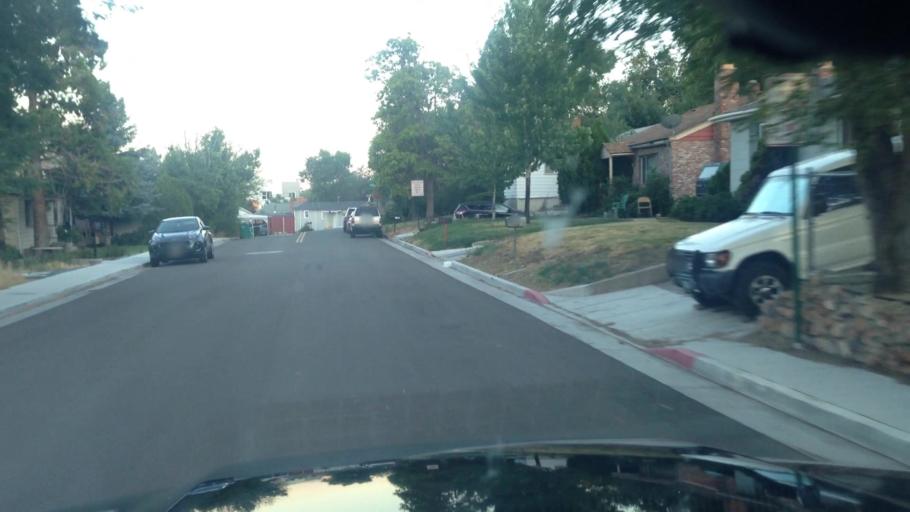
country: US
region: Nevada
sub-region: Washoe County
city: Reno
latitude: 39.5429
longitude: -119.8191
